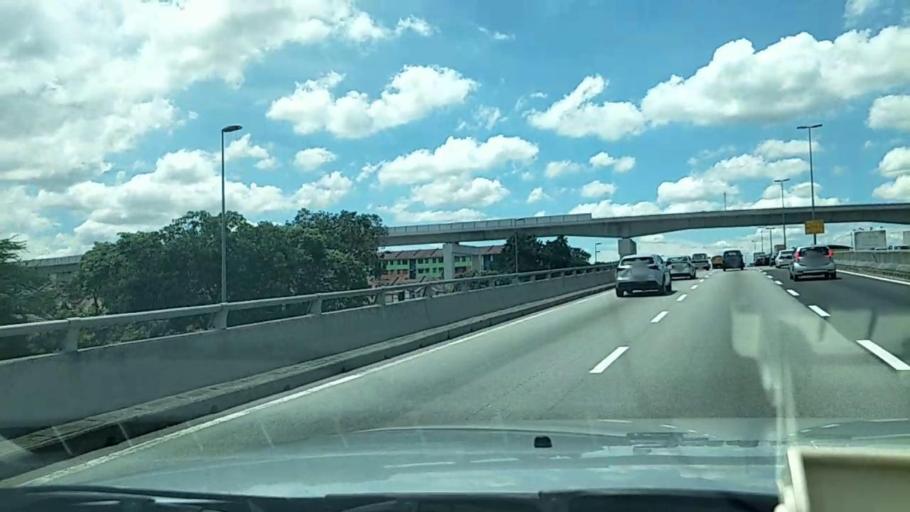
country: MY
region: Selangor
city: Subang Jaya
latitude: 3.0086
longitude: 101.6111
